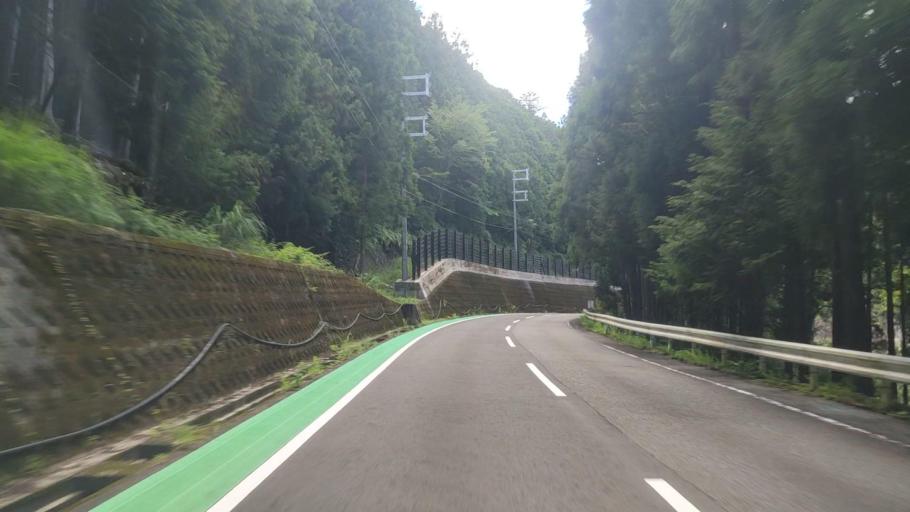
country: JP
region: Mie
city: Owase
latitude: 33.9642
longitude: 135.9931
